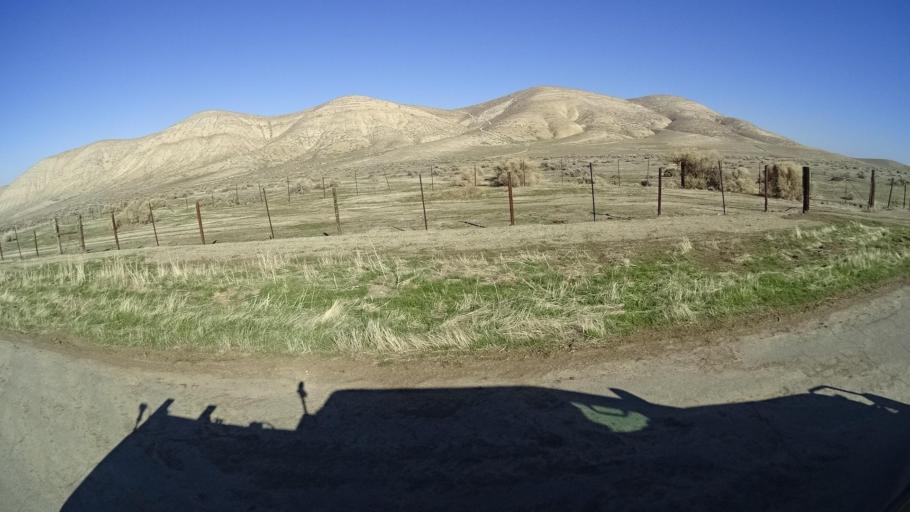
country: US
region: California
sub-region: Kern County
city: Maricopa
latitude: 34.9972
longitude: -119.3984
